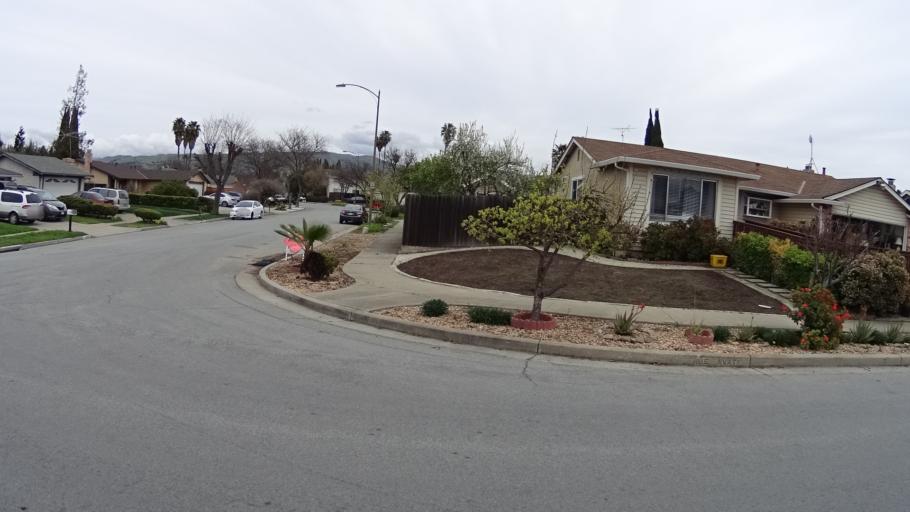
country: US
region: California
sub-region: Santa Clara County
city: San Jose
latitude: 37.3865
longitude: -121.8789
